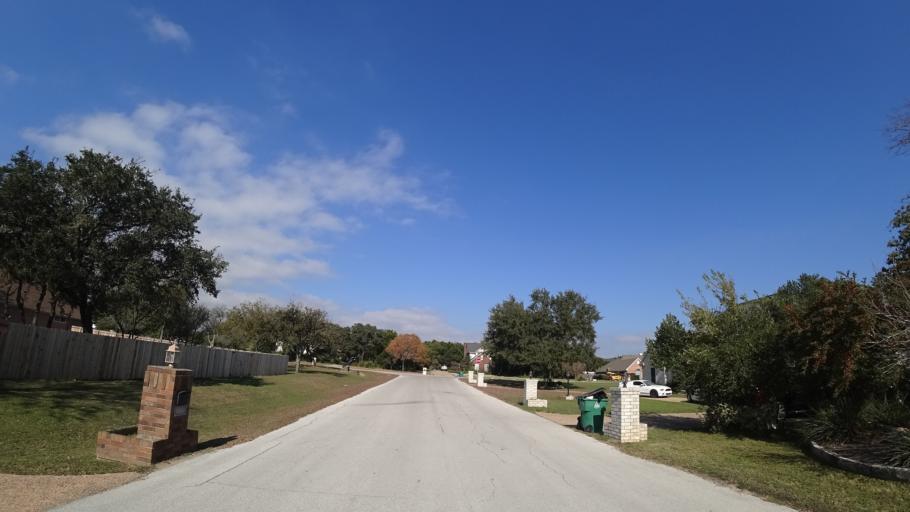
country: US
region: Texas
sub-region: Travis County
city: Shady Hollow
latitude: 30.1608
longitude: -97.8706
